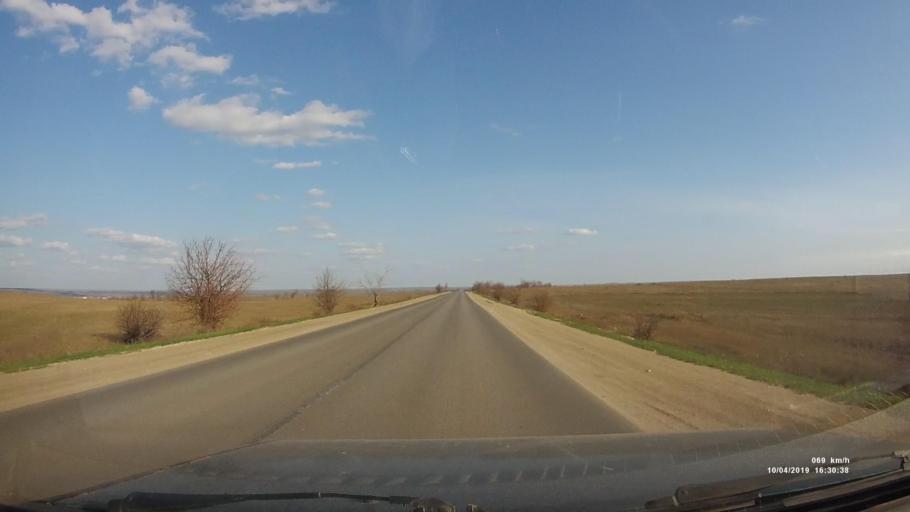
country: RU
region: Rostov
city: Staraya Stanitsa
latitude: 48.2606
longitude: 40.3672
